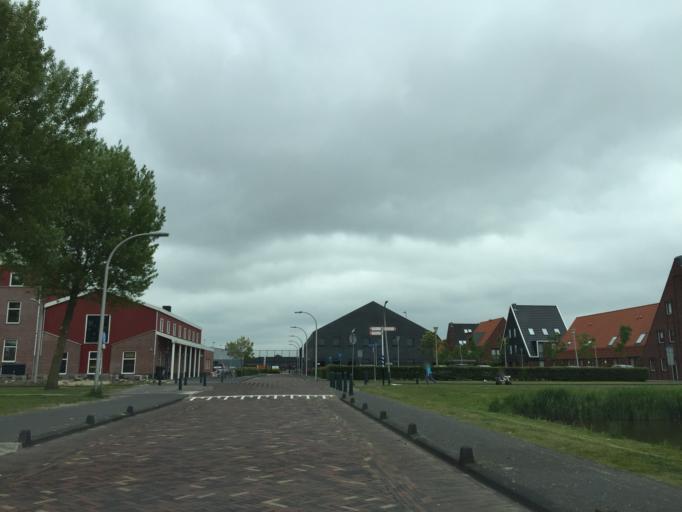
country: NL
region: South Holland
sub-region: Gemeente Den Haag
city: Ypenburg
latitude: 52.0319
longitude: 4.3836
